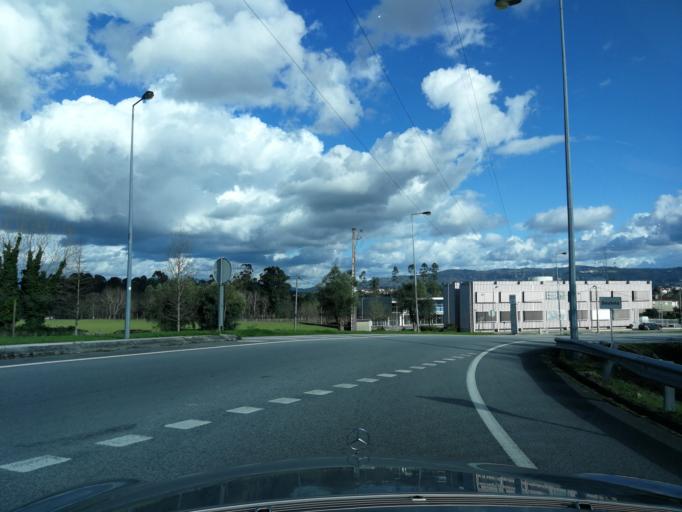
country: PT
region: Braga
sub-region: Vila Verde
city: Vila Verde
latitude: 41.6169
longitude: -8.4340
